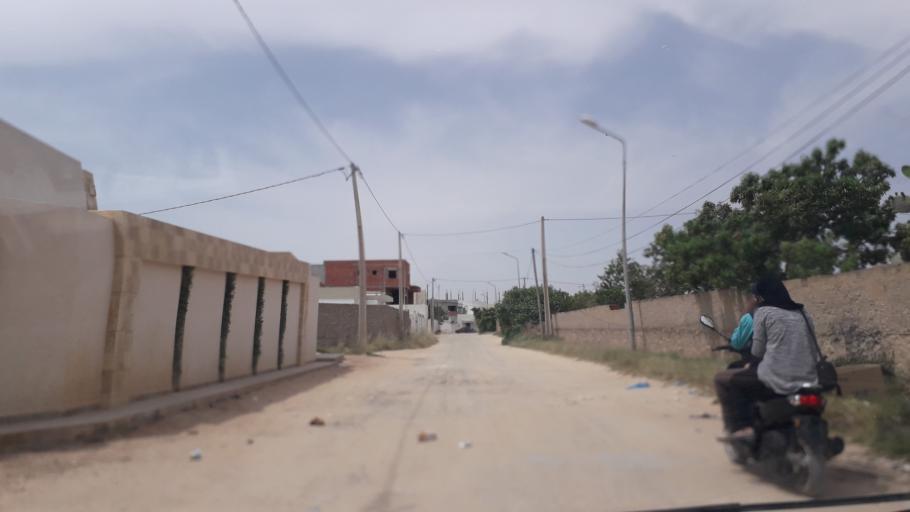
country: TN
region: Safaqis
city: Al Qarmadah
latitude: 34.8057
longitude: 10.7704
